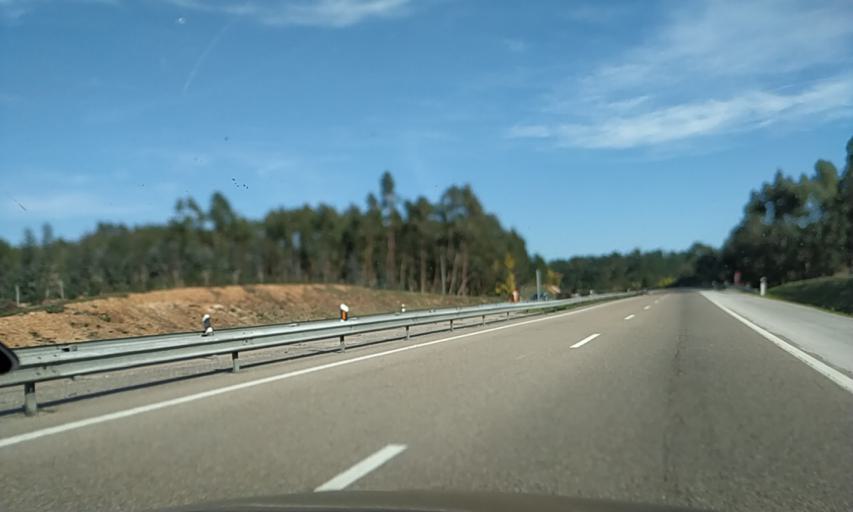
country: PT
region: Santarem
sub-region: Constancia
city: Constancia
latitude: 39.4848
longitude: -8.3747
